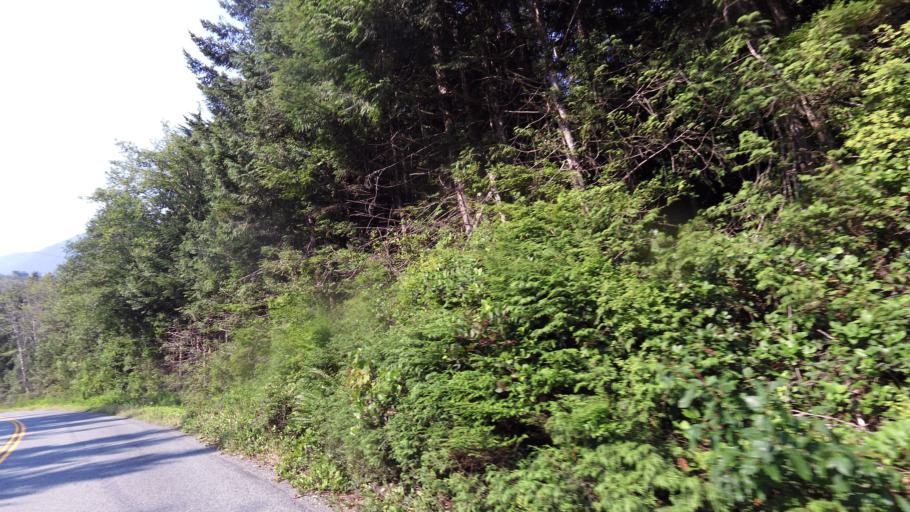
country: CA
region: British Columbia
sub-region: Regional District of Alberni-Clayoquot
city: Ucluelet
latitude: 49.1036
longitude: -125.4535
